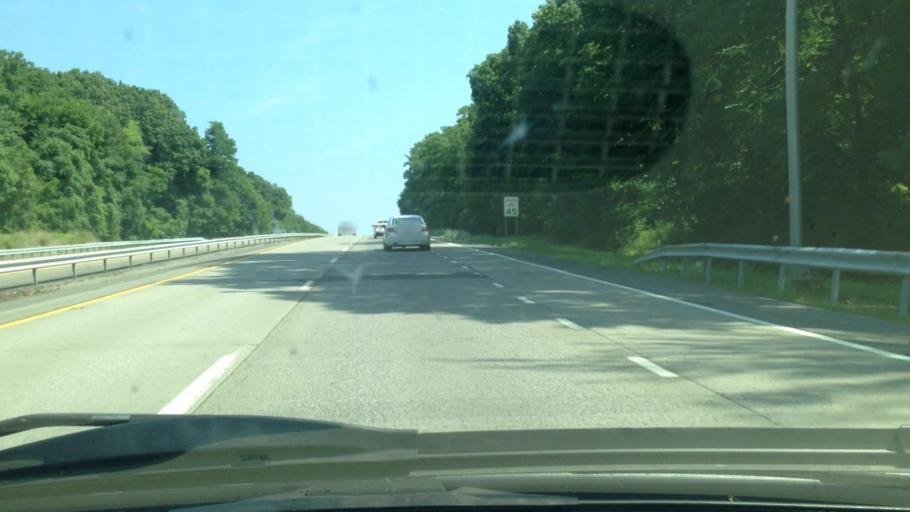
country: US
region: New York
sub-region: Ulster County
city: Kingston
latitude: 41.9323
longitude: -73.9850
